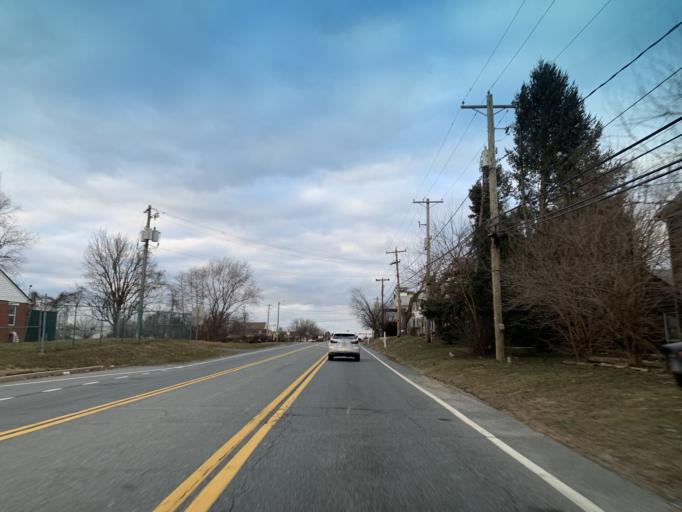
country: US
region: Delaware
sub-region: New Castle County
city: Bear
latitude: 39.6291
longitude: -75.6606
